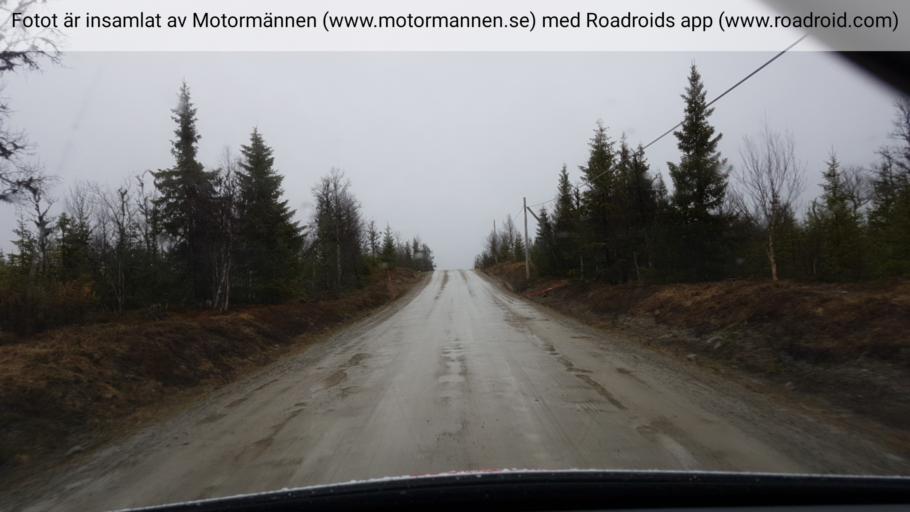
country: SE
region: Jaemtland
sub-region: Are Kommun
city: Jarpen
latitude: 62.5990
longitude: 13.2859
